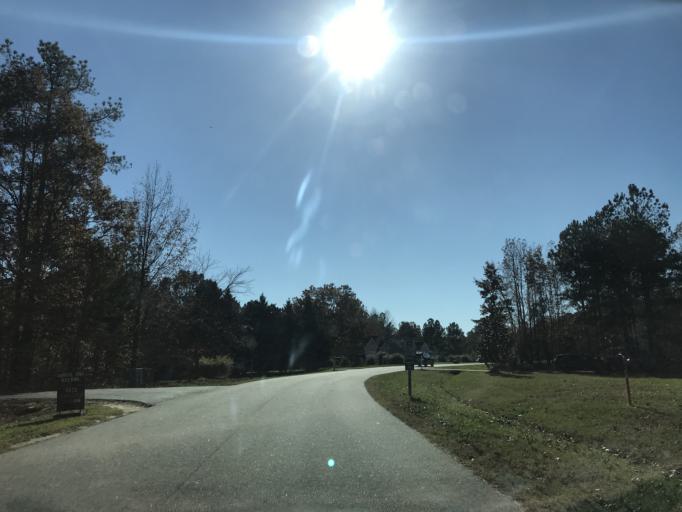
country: US
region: North Carolina
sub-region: Wake County
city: Rolesville
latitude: 35.9746
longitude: -78.3642
